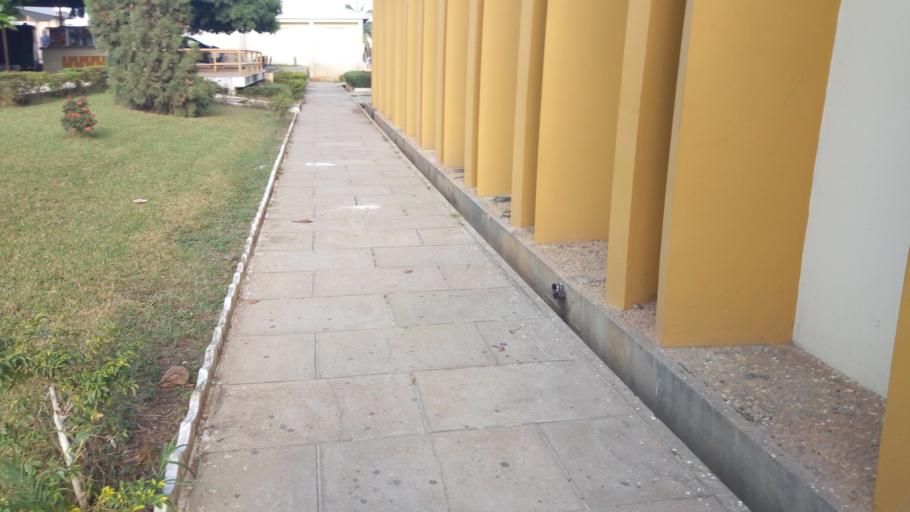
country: GH
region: Ashanti
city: Mamponteng
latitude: 6.6744
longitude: -1.5648
